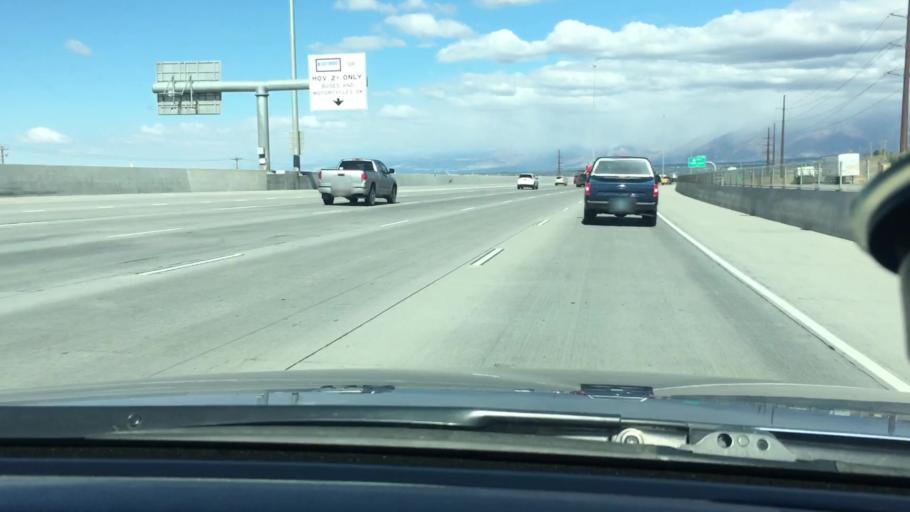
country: US
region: Utah
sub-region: Salt Lake County
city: Bluffdale
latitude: 40.4641
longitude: -111.9131
